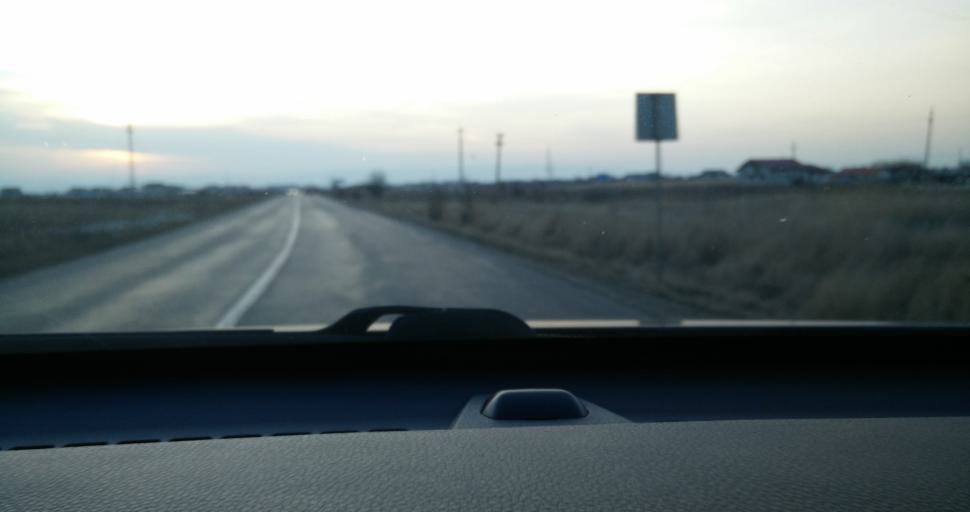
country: RO
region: Vrancea
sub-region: Comuna Milcovul
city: Milcovul
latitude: 45.6771
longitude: 27.2503
